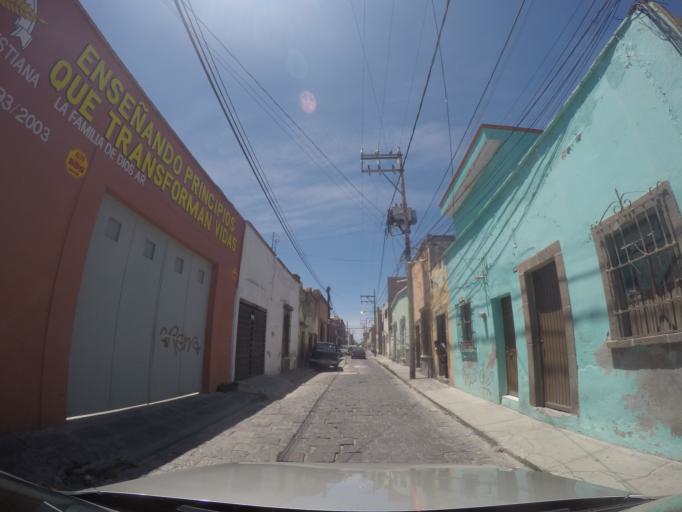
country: MX
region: San Luis Potosi
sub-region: San Luis Potosi
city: San Luis Potosi
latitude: 22.1563
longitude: -100.9817
